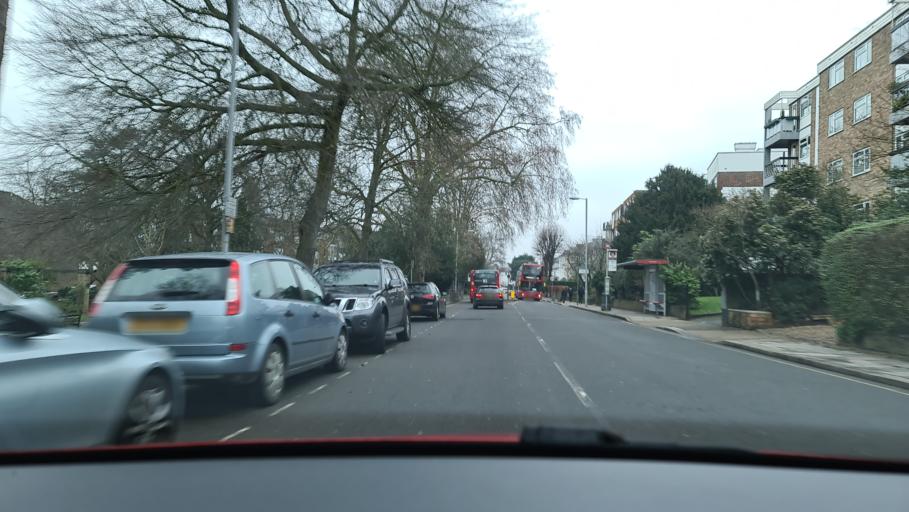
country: GB
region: England
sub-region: Greater London
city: Surbiton
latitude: 51.3952
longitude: -0.3042
